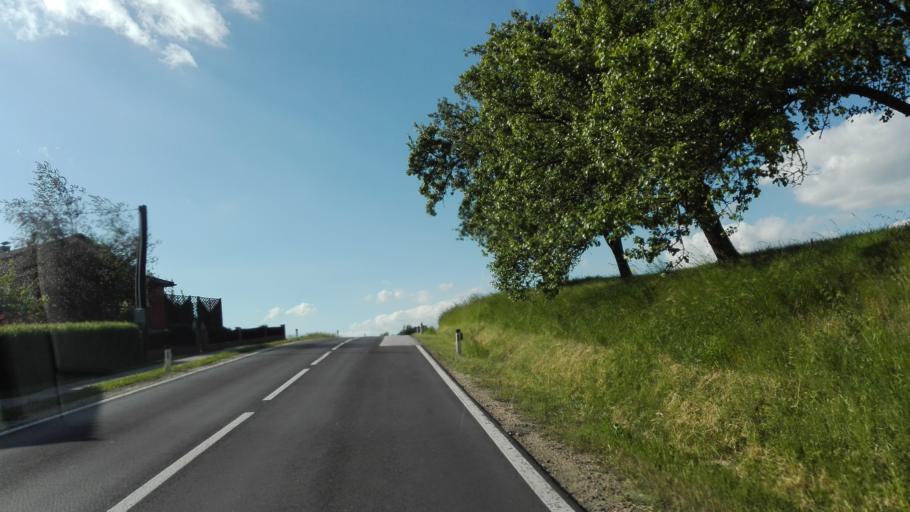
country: AT
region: Upper Austria
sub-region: Politischer Bezirk Urfahr-Umgebung
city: Engerwitzdorf
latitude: 48.3377
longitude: 14.5158
